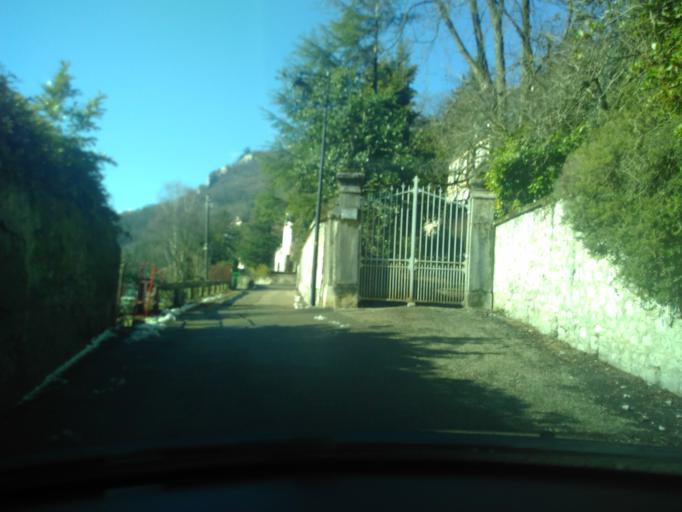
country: FR
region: Rhone-Alpes
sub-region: Departement de l'Isere
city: La Tronche
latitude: 45.2048
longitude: 5.7356
